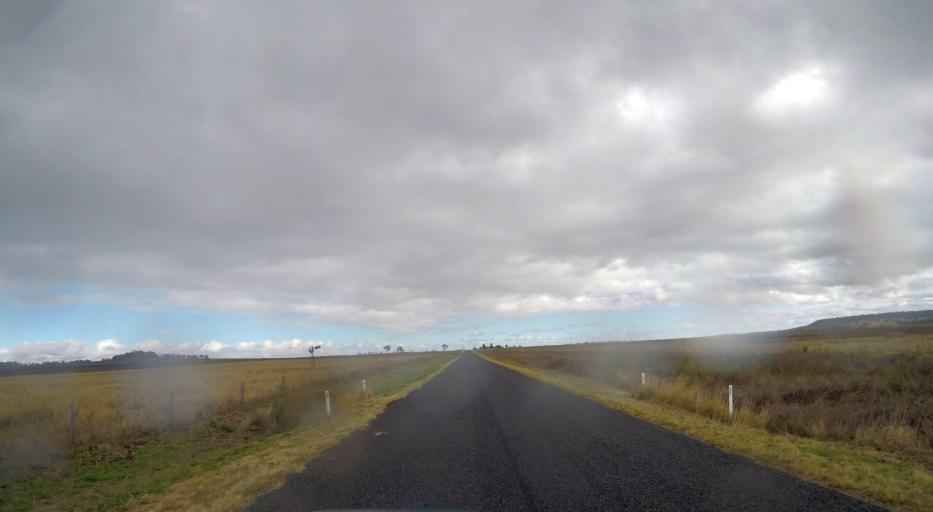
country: AU
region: Queensland
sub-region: Southern Downs
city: Warwick
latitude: -28.0486
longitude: 152.0406
